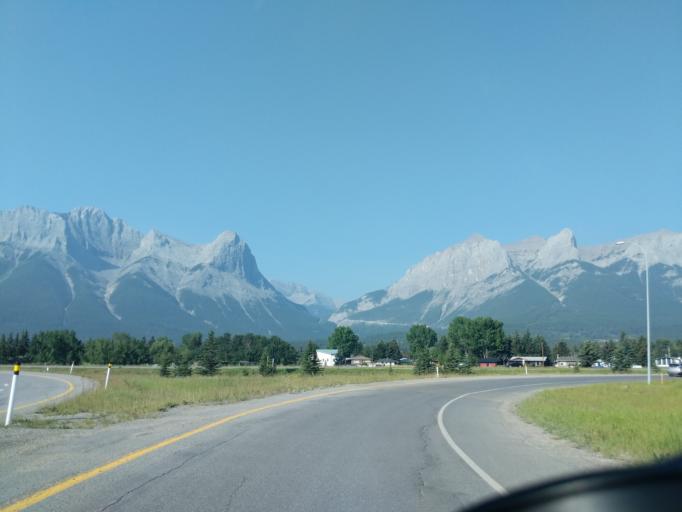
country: CA
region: Alberta
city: Canmore
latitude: 51.0957
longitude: -115.3489
